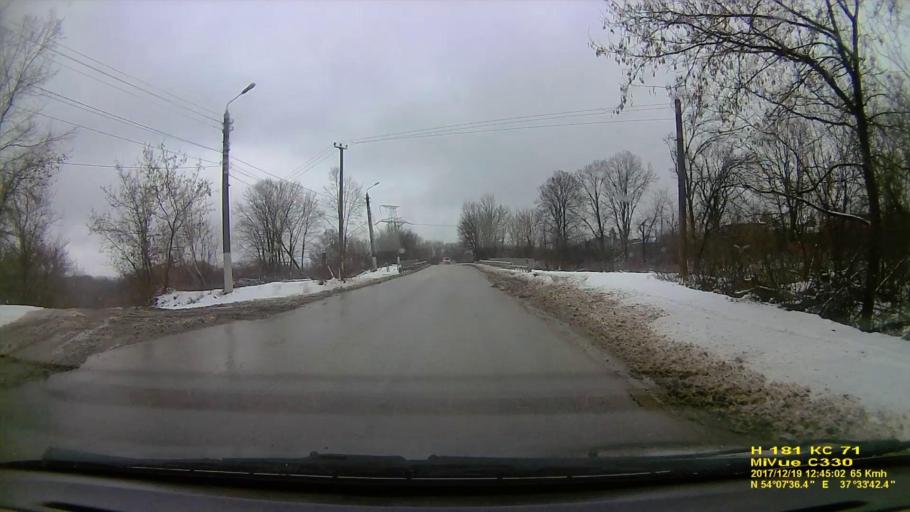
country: RU
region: Tula
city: Kosaya Gora
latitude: 54.1269
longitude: 37.5619
